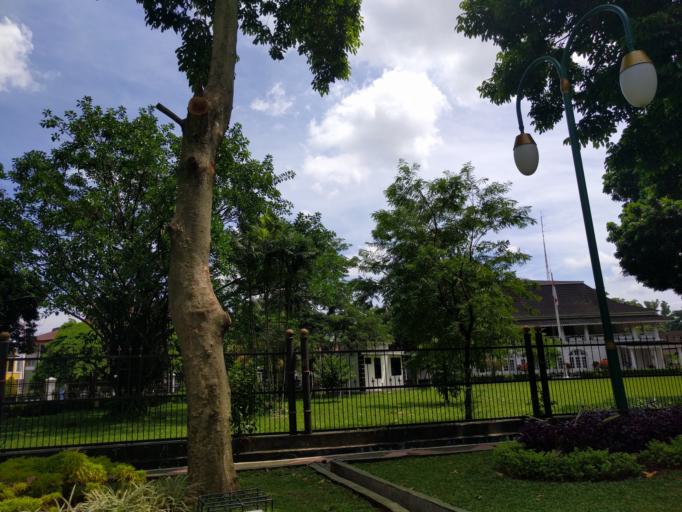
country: ID
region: West Java
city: Bogor
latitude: -6.5943
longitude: 106.7950
